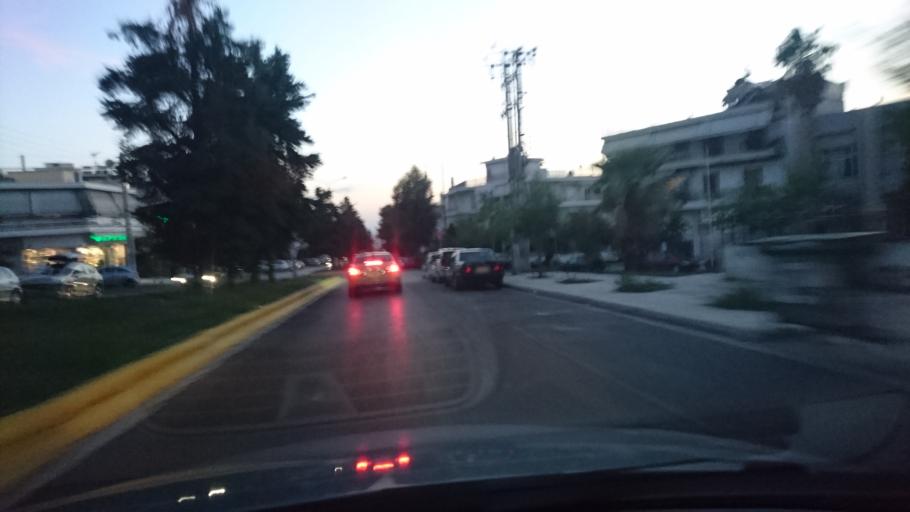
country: GR
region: Attica
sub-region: Nomarchia Athinas
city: Argyroupoli
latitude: 37.9180
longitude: 23.7475
